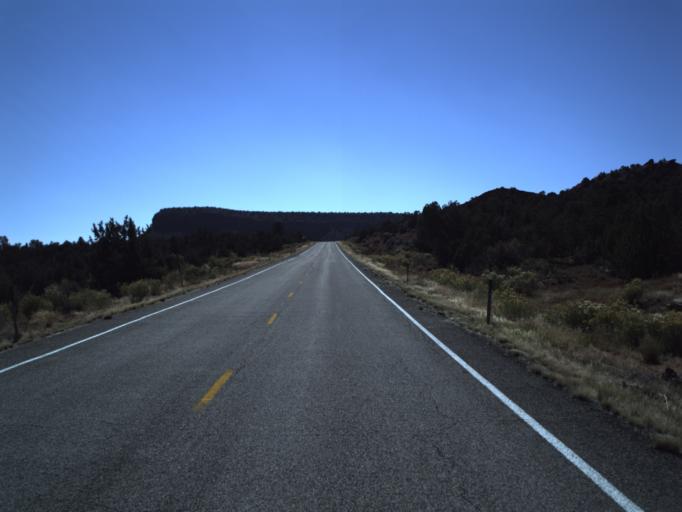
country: US
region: Utah
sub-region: San Juan County
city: Blanding
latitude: 37.5795
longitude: -110.0390
